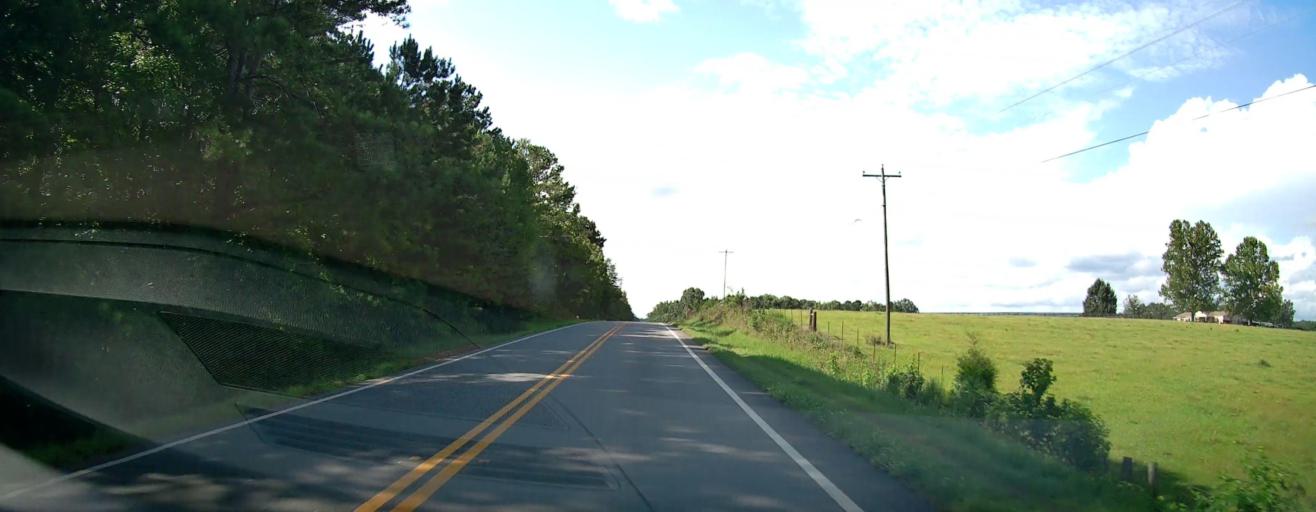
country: US
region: Georgia
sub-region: Upson County
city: Hannahs Mill
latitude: 32.9519
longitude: -84.4593
